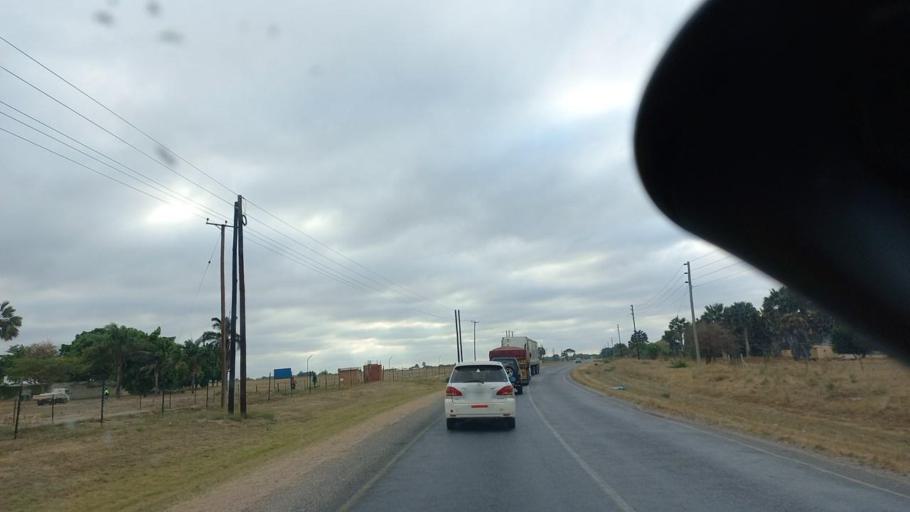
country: ZM
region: Lusaka
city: Chongwe
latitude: -15.3426
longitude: 28.5214
